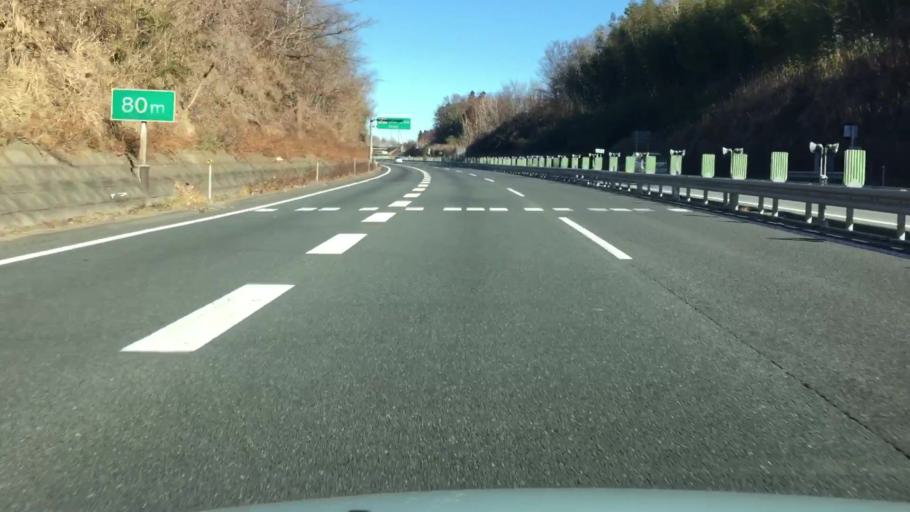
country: JP
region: Gunma
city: Shibukawa
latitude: 36.5192
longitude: 139.0378
